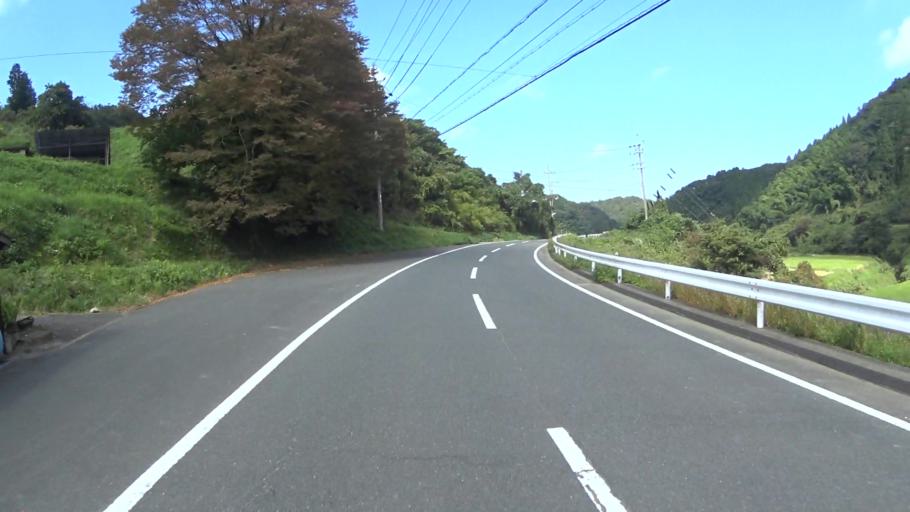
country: JP
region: Kyoto
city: Miyazu
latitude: 35.6989
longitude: 135.2497
